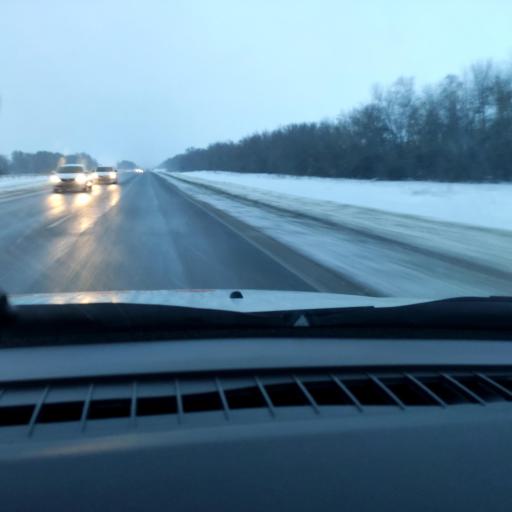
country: RU
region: Samara
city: Dubovyy Umet
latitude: 53.0368
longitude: 50.2124
